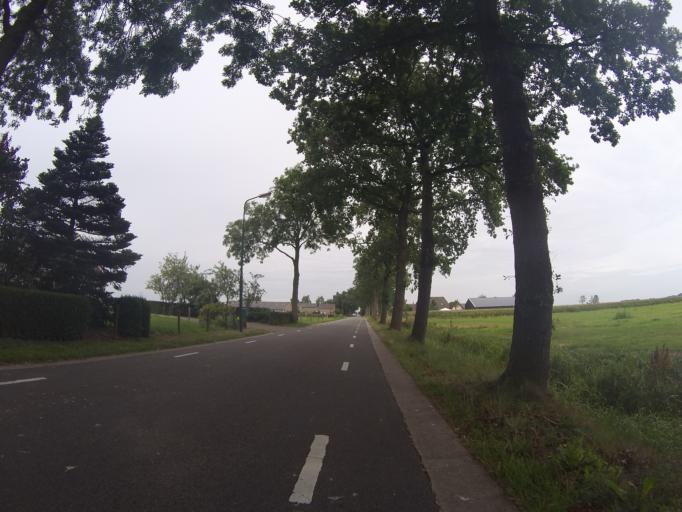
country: NL
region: Utrecht
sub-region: Gemeente Bunschoten
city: Bunschoten
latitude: 52.2123
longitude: 5.3890
